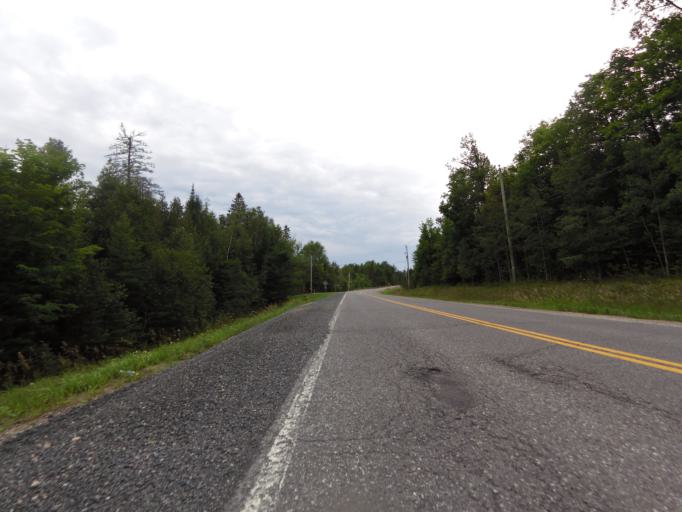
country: CA
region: Ontario
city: Carleton Place
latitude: 45.1196
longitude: -76.3500
